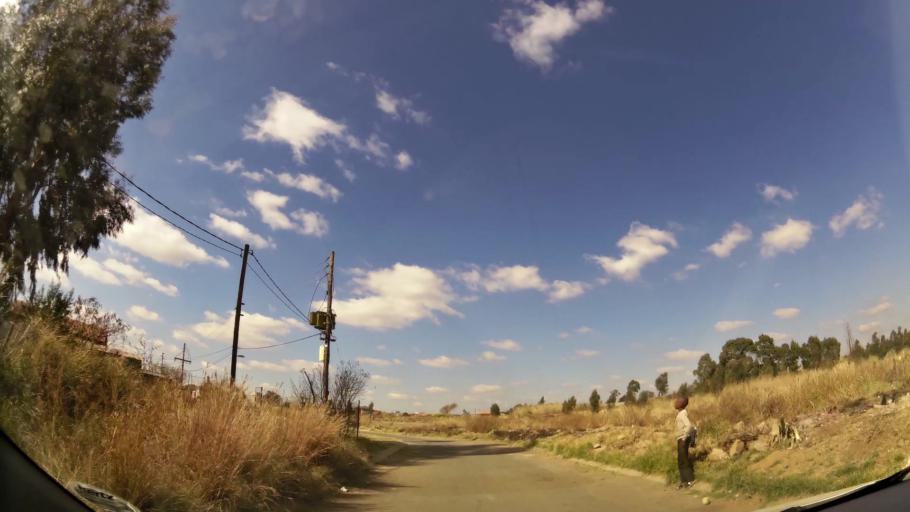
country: ZA
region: Gauteng
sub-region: West Rand District Municipality
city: Krugersdorp
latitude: -26.1460
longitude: 27.7821
